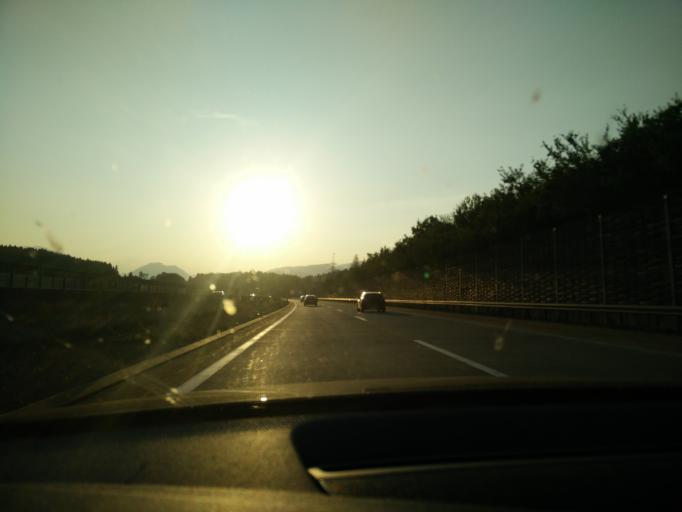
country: AT
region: Carinthia
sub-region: Politischer Bezirk Villach Land
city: Wernberg
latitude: 46.6229
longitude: 13.9728
